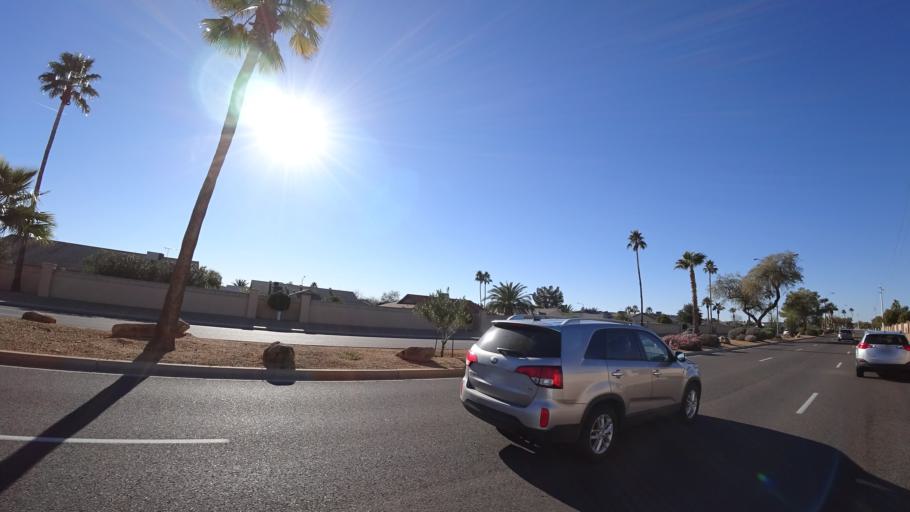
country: US
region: Arizona
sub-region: Maricopa County
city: Sun City West
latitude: 33.6674
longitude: -112.3668
